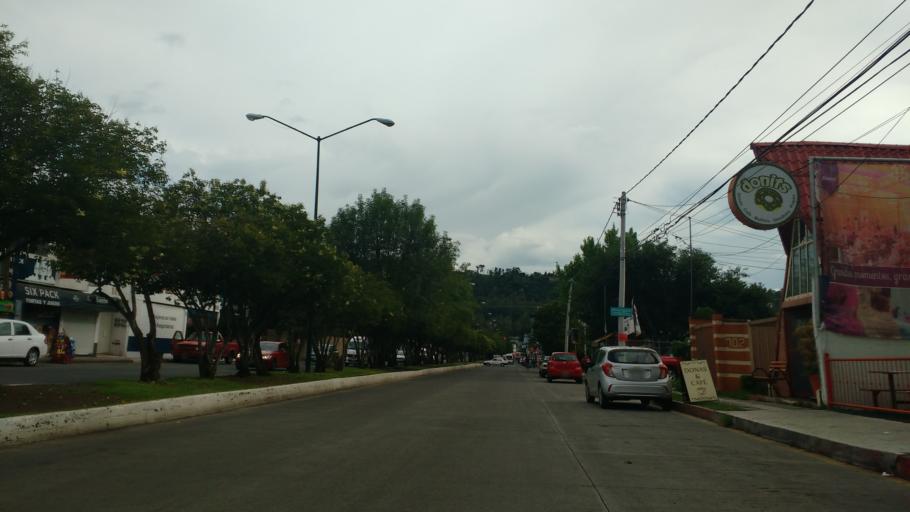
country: MX
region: Michoacan
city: Morelia
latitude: 19.6888
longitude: -101.1726
